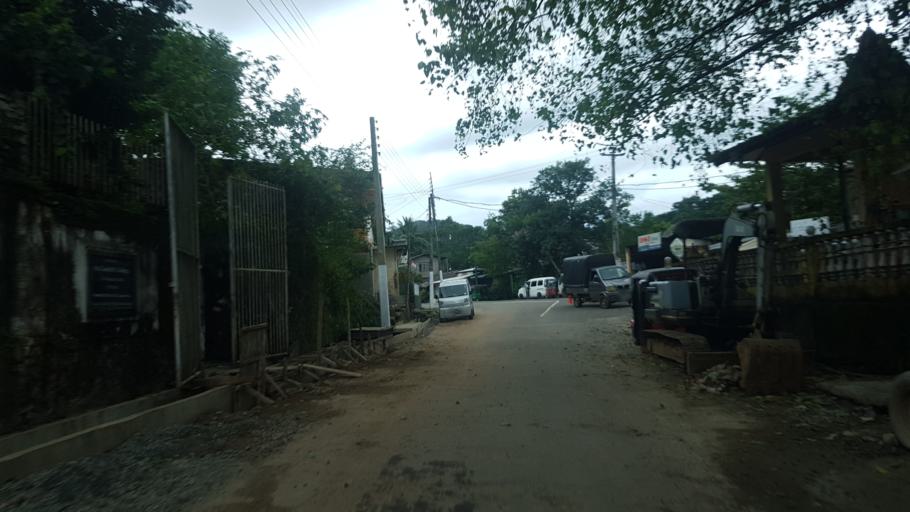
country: LK
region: Western
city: Hanwella Ihala
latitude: 7.0273
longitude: 80.2956
